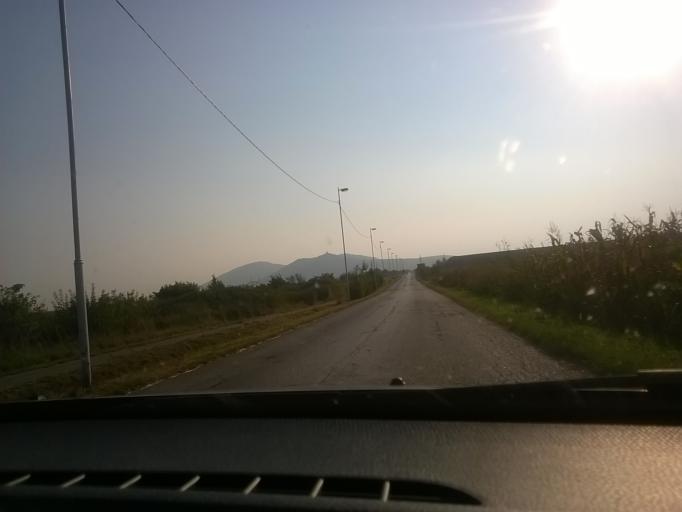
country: RS
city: Pavlis
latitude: 45.1118
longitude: 21.2552
